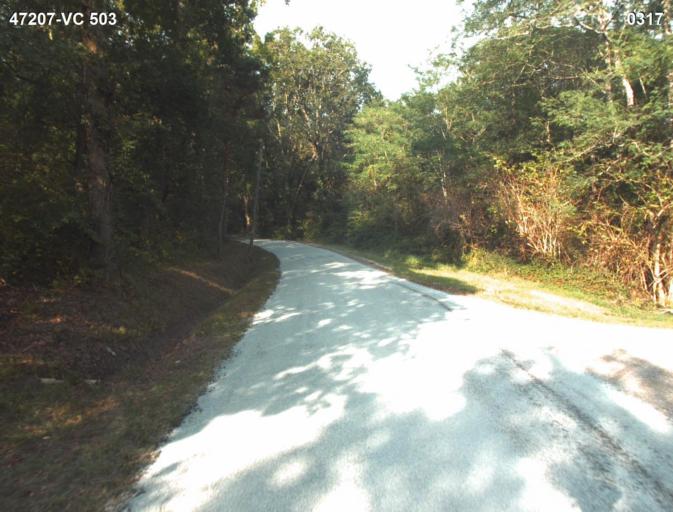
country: FR
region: Aquitaine
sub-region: Departement du Lot-et-Garonne
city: Barbaste
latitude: 44.2036
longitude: 0.2336
